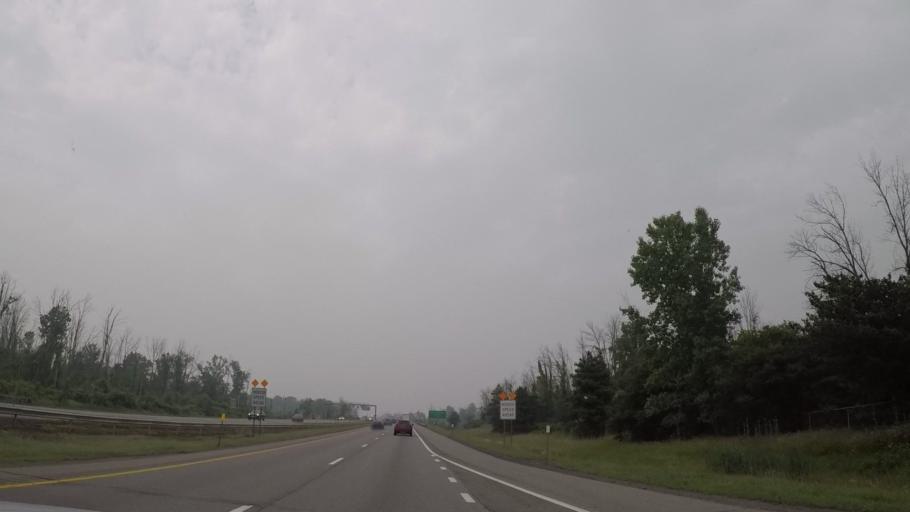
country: US
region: New York
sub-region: Erie County
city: Grandyle Village
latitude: 43.0560
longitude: -78.9904
